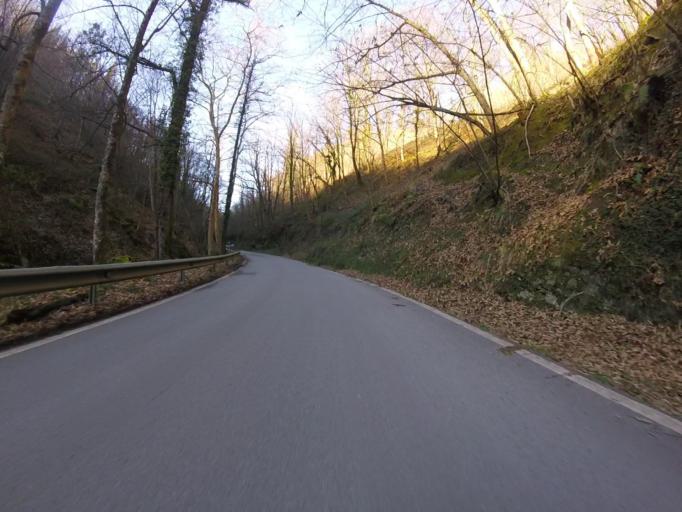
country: ES
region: Navarre
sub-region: Provincia de Navarra
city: Lesaka
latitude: 43.2503
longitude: -1.7208
